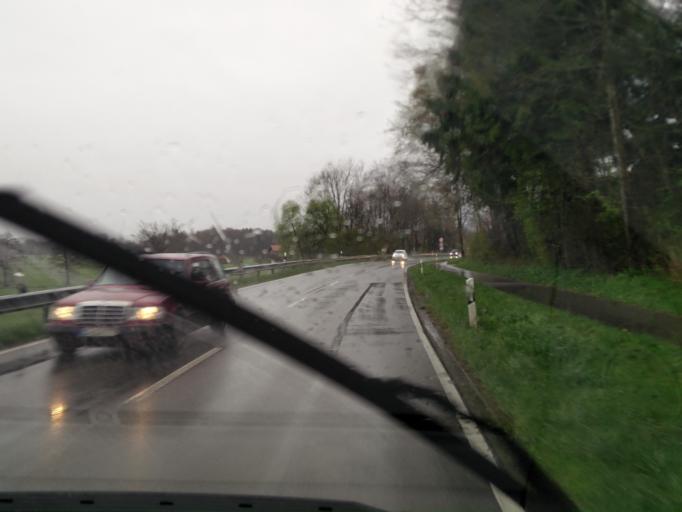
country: DE
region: Bavaria
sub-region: Upper Bavaria
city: Bernau am Chiemsee
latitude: 47.8021
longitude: 12.3869
